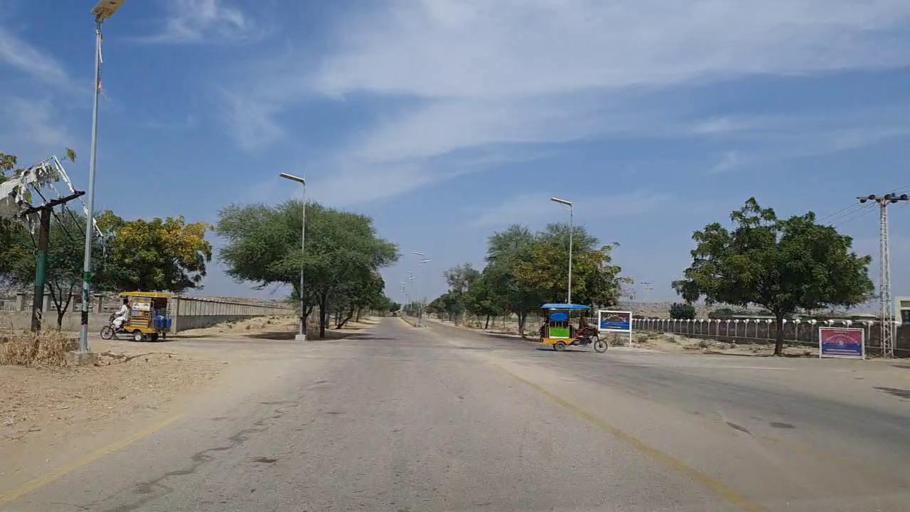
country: PK
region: Sindh
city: Mithi
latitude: 24.7508
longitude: 69.7954
